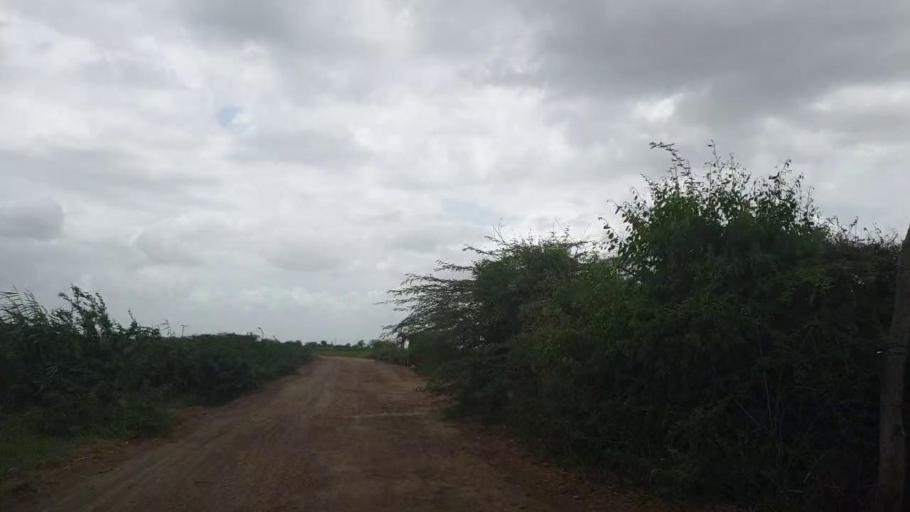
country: PK
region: Sindh
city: Badin
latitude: 24.6539
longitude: 68.9461
